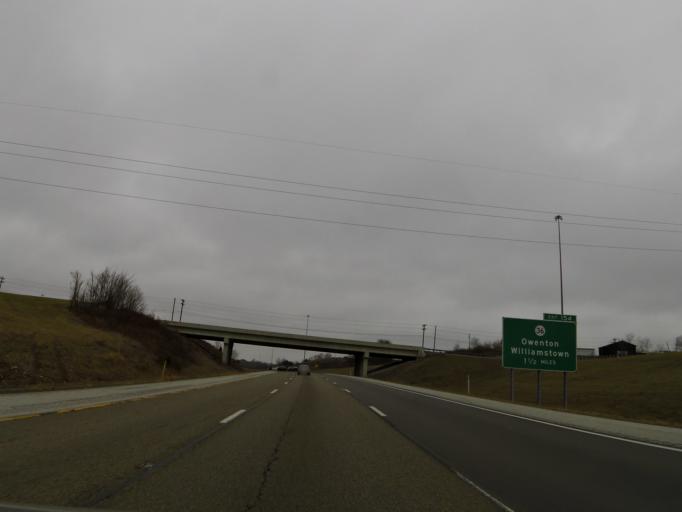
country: US
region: Kentucky
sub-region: Grant County
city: Williamstown
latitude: 38.6479
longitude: -84.5876
